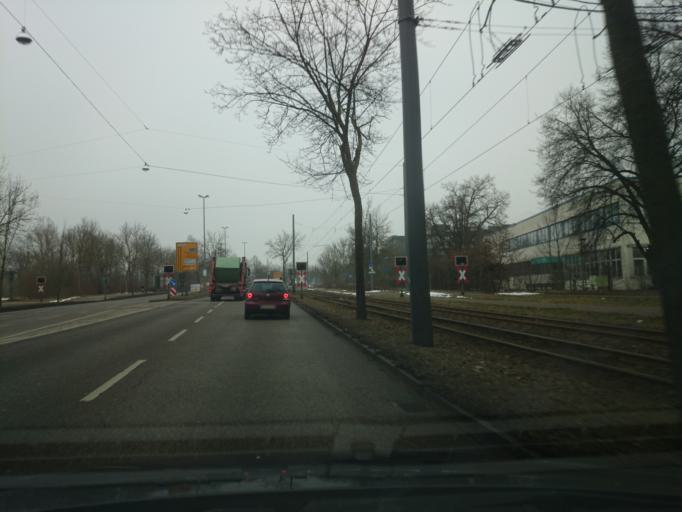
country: DE
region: Bavaria
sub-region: Swabia
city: Augsburg
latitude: 48.3391
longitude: 10.9072
